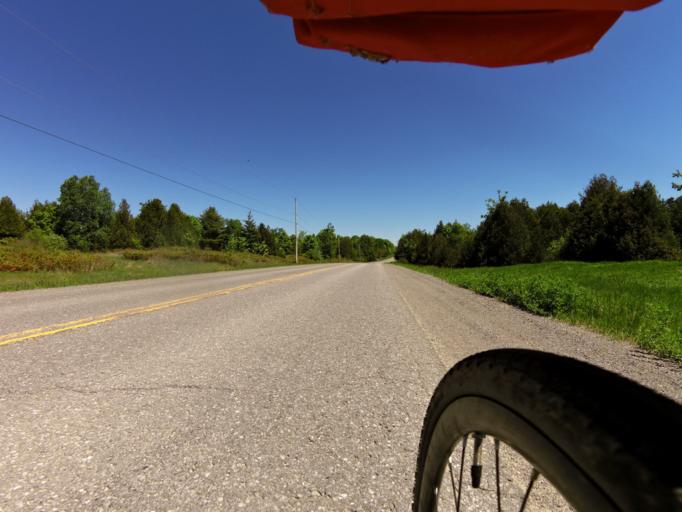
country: CA
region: Ontario
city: Carleton Place
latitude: 45.1841
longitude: -76.3789
